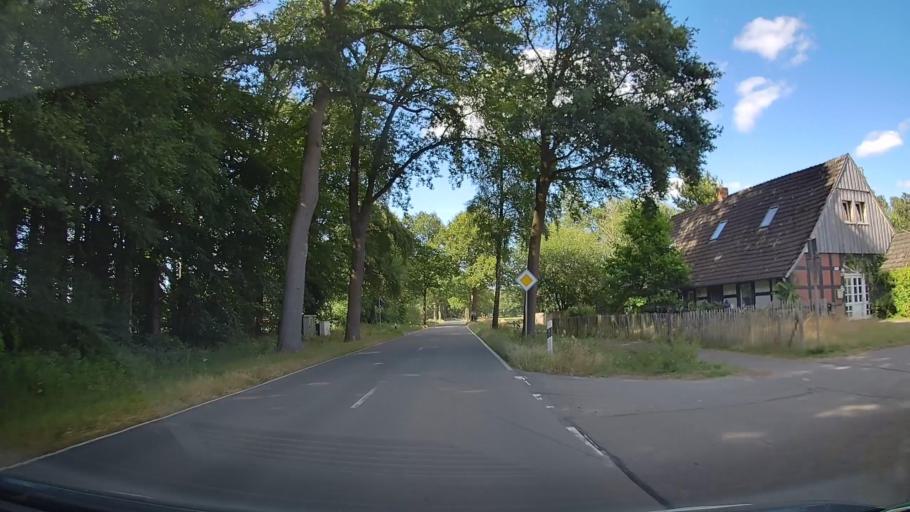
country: DE
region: Lower Saxony
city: Menslage
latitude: 52.6476
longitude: 7.8106
